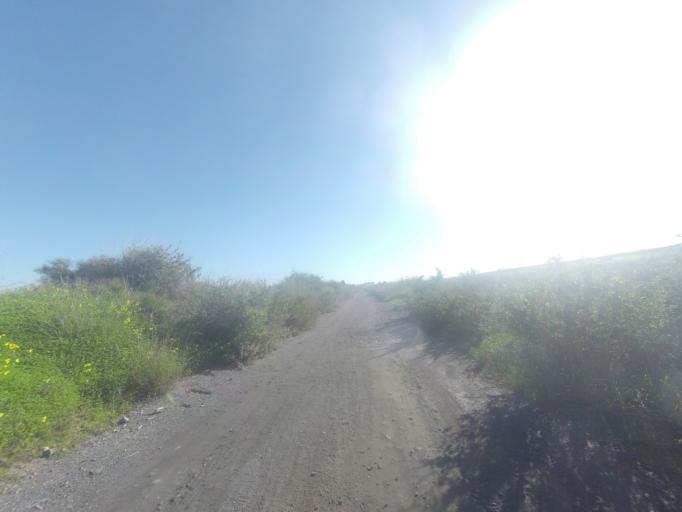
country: ES
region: Andalusia
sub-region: Provincia de Huelva
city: Palos de la Frontera
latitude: 37.2552
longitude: -6.9106
